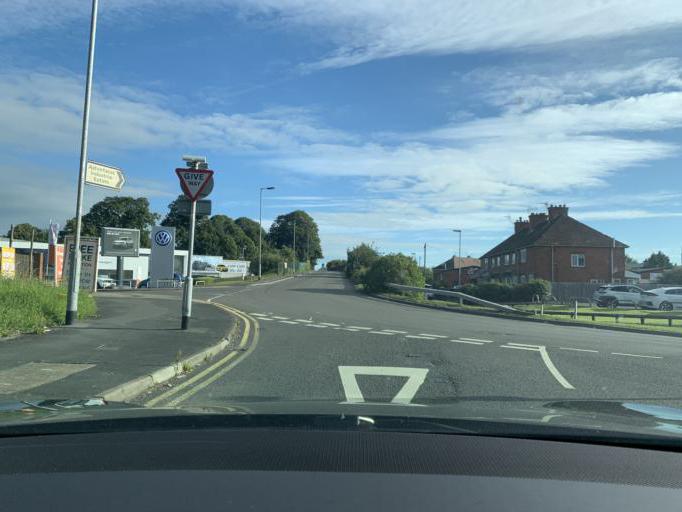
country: GB
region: England
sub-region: Staffordshire
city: Stafford
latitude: 52.8198
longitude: -2.1183
